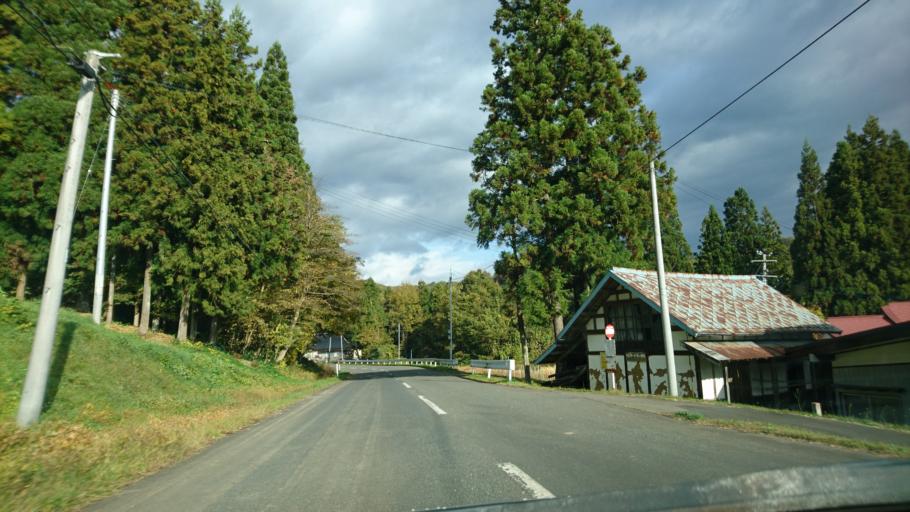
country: JP
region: Iwate
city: Mizusawa
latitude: 39.0934
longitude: 140.9739
